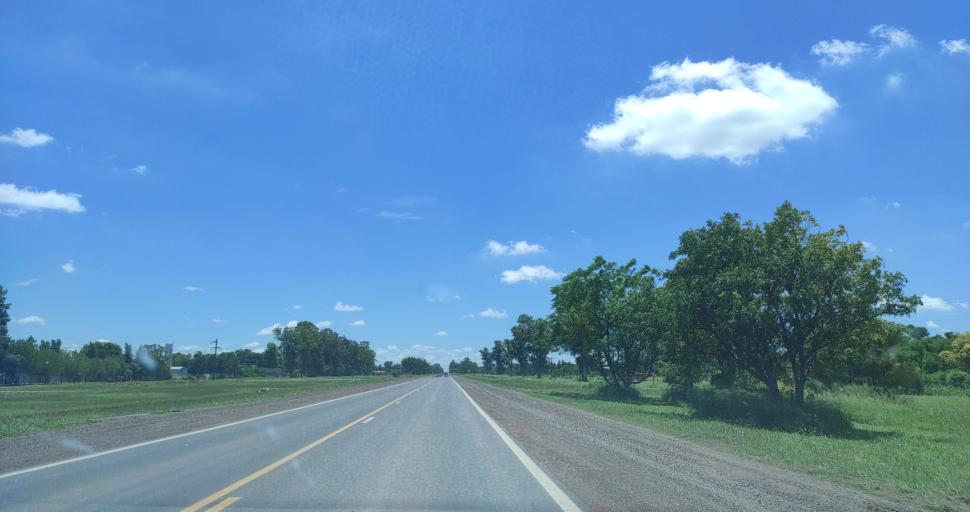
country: AR
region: Chaco
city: Las Brenas
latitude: -27.1105
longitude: -61.0760
